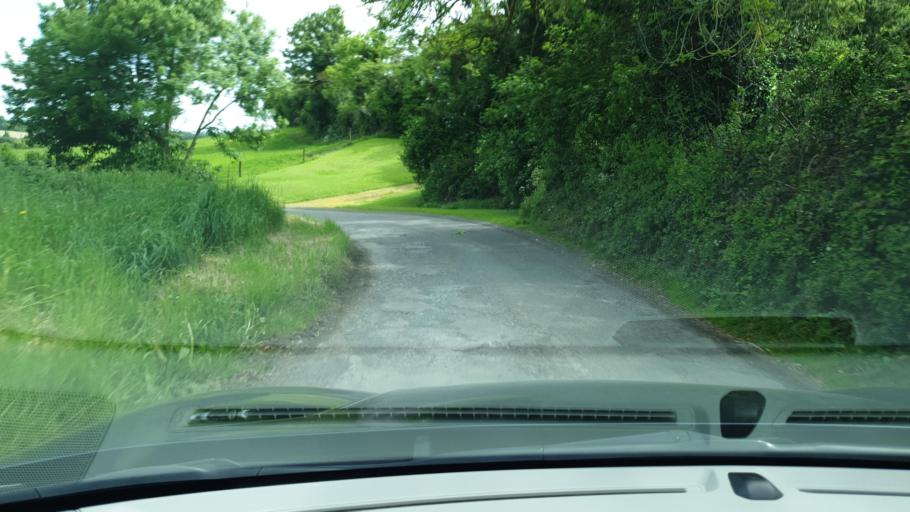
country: IE
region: Ulster
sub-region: An Cabhan
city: Kingscourt
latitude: 53.7974
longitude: -6.7218
